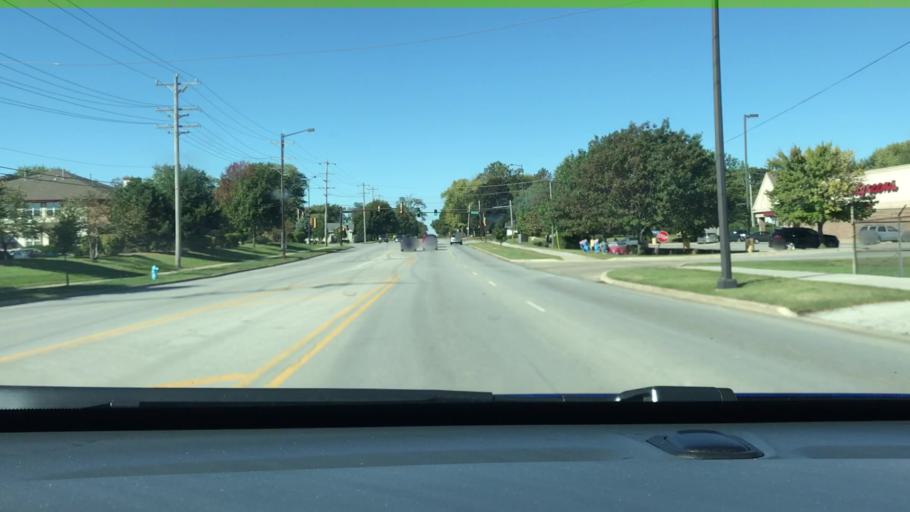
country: US
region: Illinois
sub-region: Kane County
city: North Aurora
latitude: 41.7812
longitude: -88.3478
